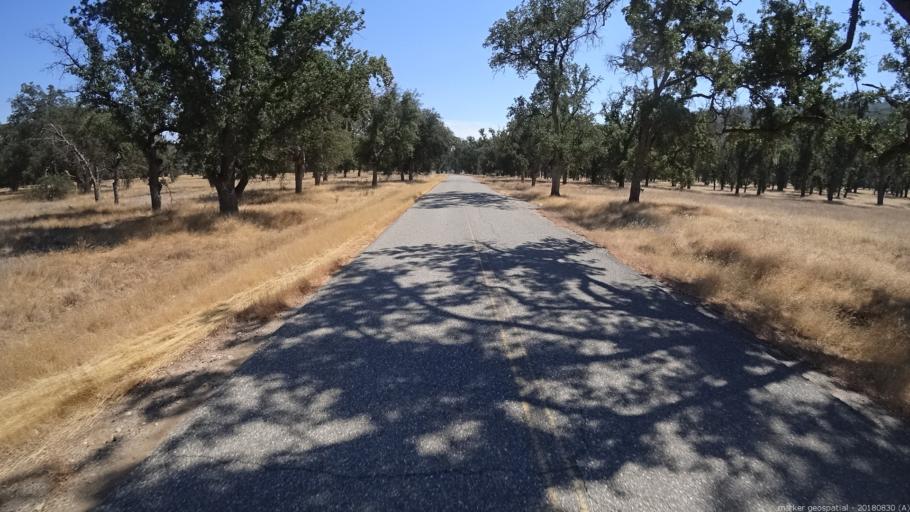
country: US
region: California
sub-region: Monterey County
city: King City
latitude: 36.0554
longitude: -121.3065
